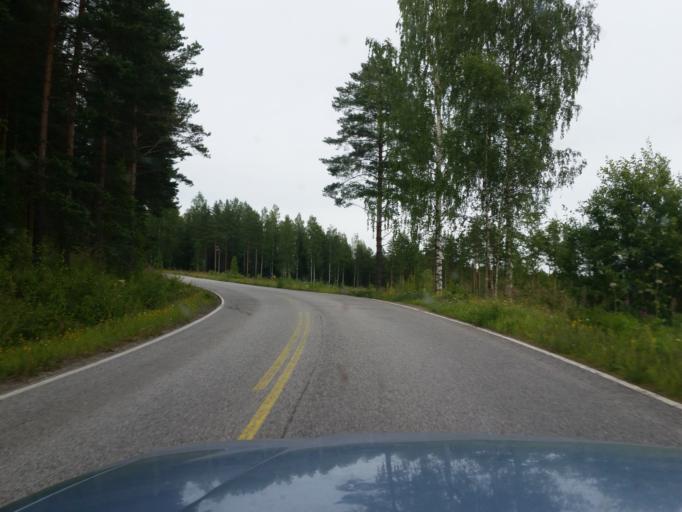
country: FI
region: Uusimaa
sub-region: Helsinki
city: Kaerkoelae
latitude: 60.5206
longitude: 23.9630
